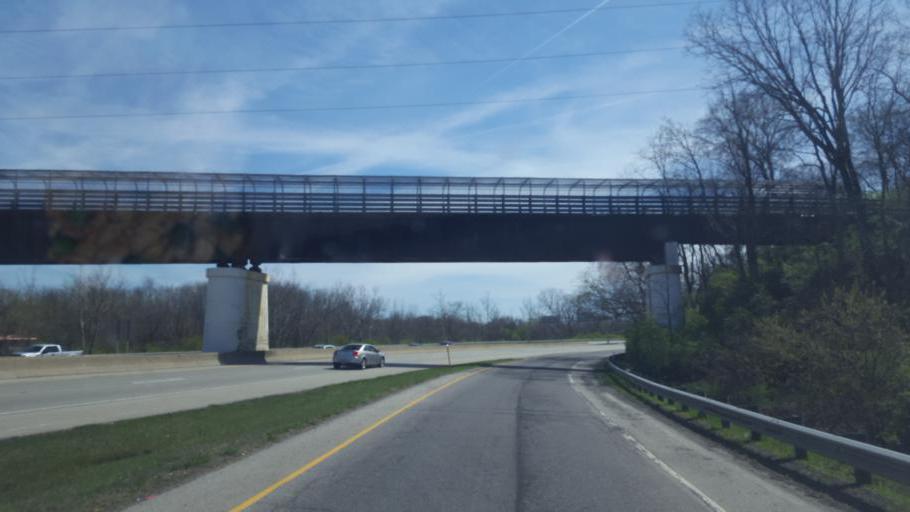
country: US
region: Ohio
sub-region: Delaware County
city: Delaware
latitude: 40.2965
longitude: -83.0620
